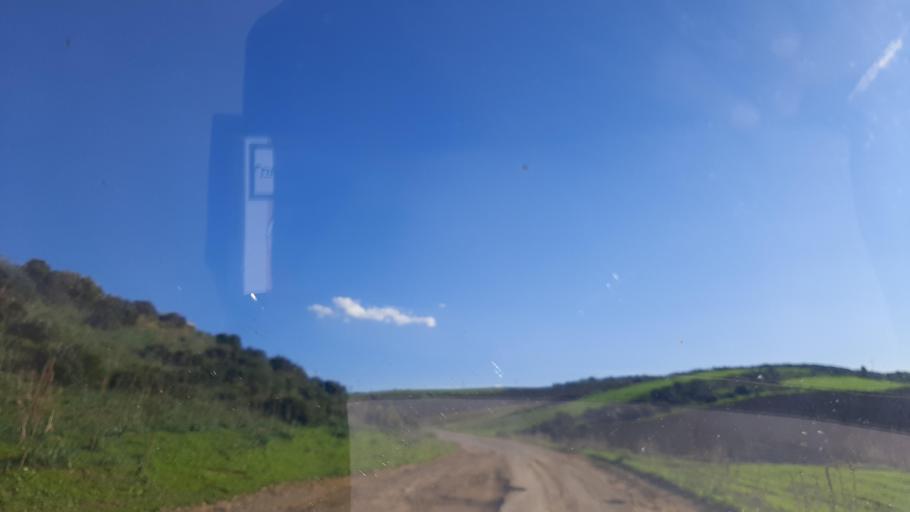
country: TN
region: Nabul
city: El Mida
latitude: 36.8129
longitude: 10.8434
